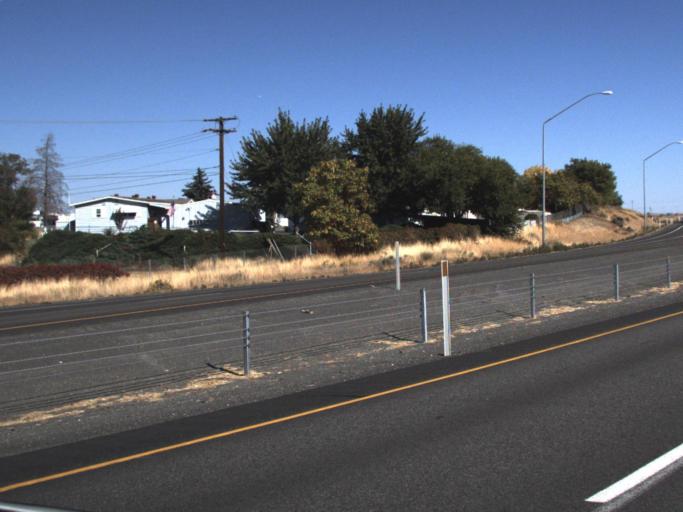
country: US
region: Washington
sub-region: Franklin County
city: Pasco
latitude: 46.2485
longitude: -119.1021
